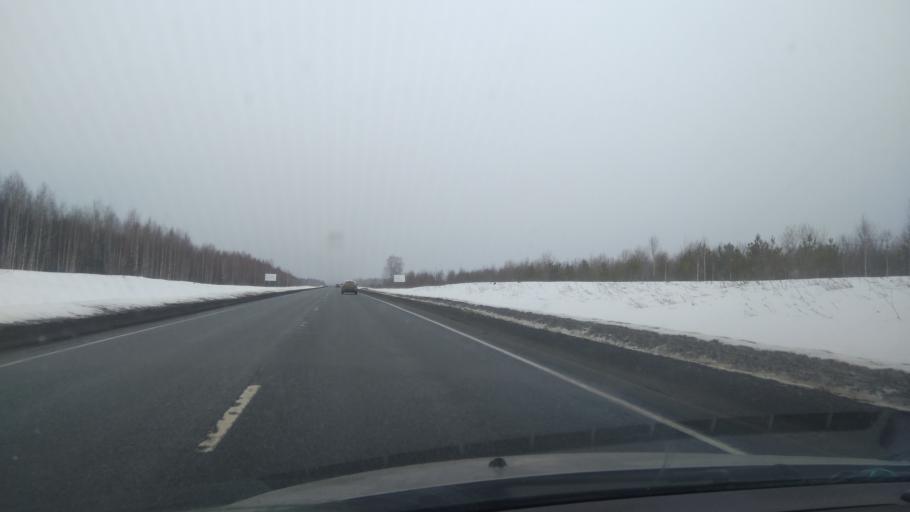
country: RU
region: Perm
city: Orda
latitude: 57.2391
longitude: 57.0580
